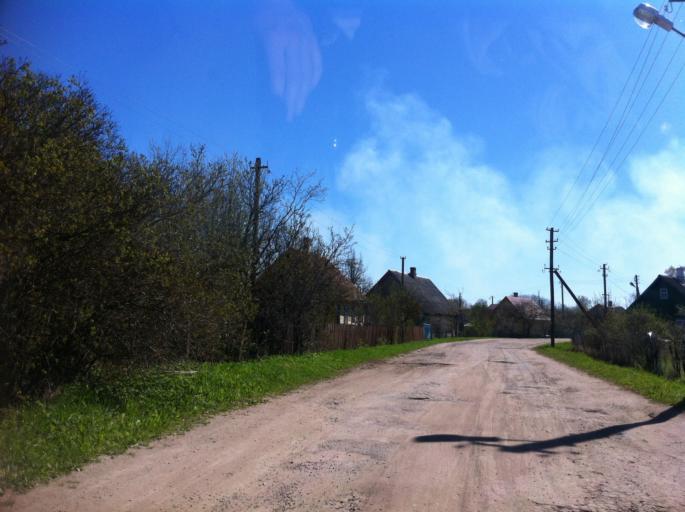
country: RU
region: Pskov
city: Izborsk
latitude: 57.7783
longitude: 27.9643
